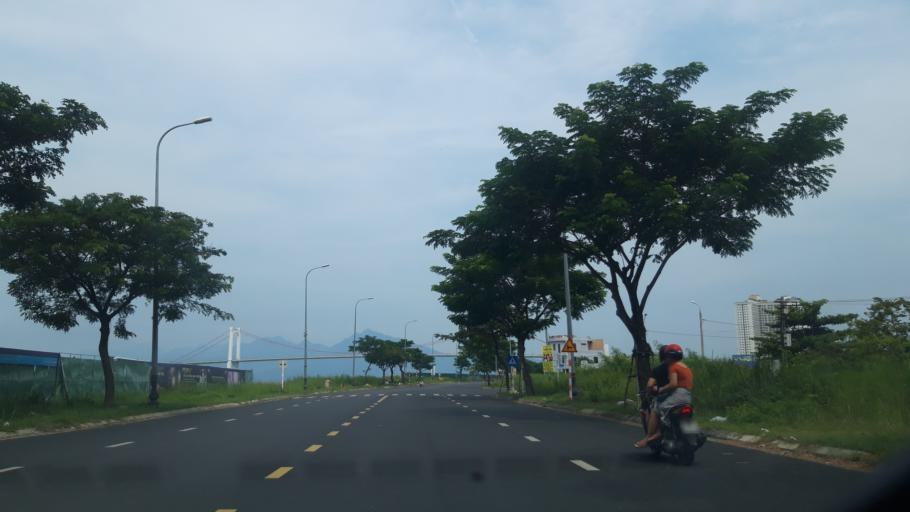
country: VN
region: Da Nang
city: Da Nang
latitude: 16.0893
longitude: 108.2279
